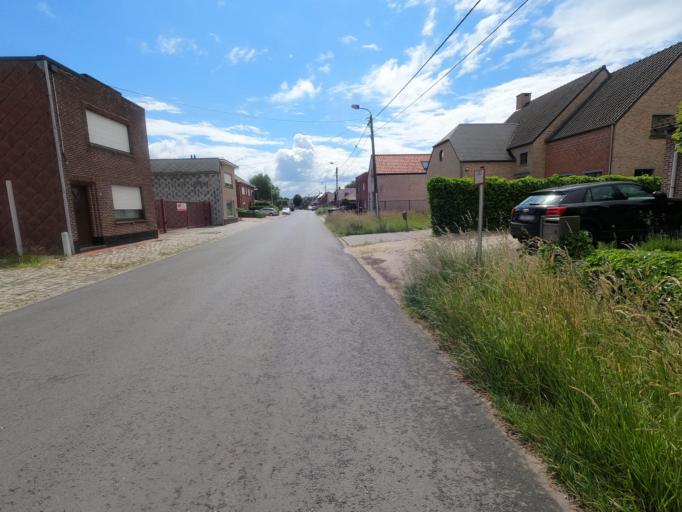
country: BE
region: Flanders
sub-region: Provincie Antwerpen
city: Berlaar
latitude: 51.0813
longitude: 4.6676
